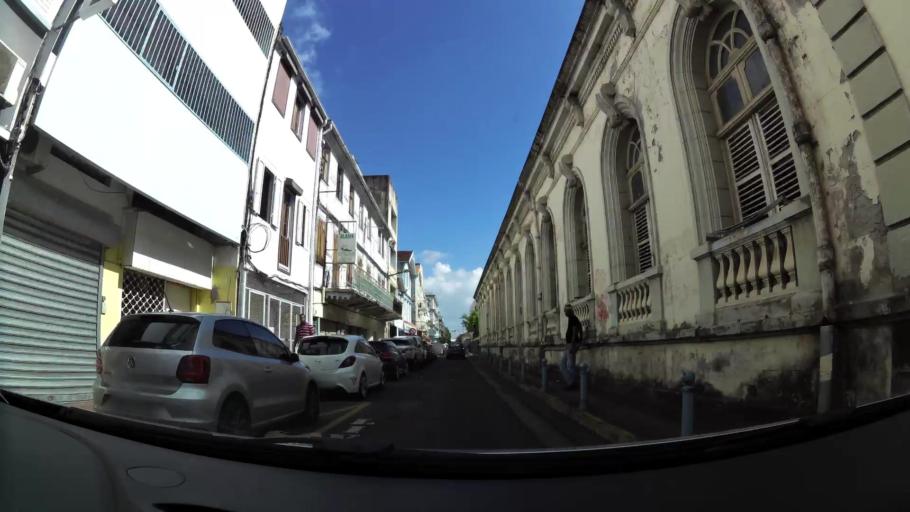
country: MQ
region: Martinique
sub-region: Martinique
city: Fort-de-France
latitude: 14.6055
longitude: -61.0700
